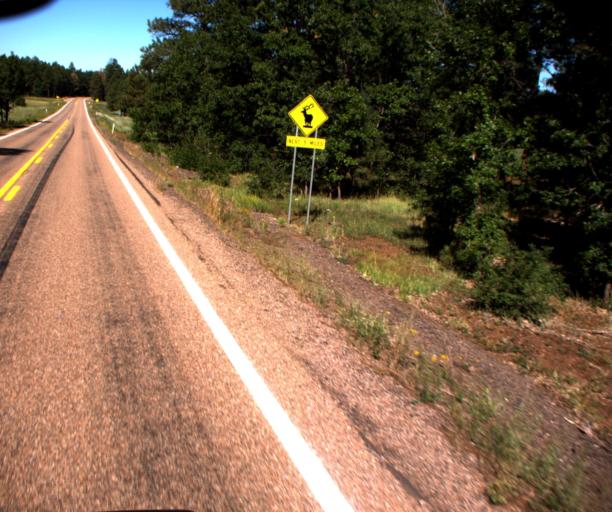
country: US
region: Arizona
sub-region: Navajo County
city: Pinetop-Lakeside
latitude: 34.0726
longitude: -109.8378
